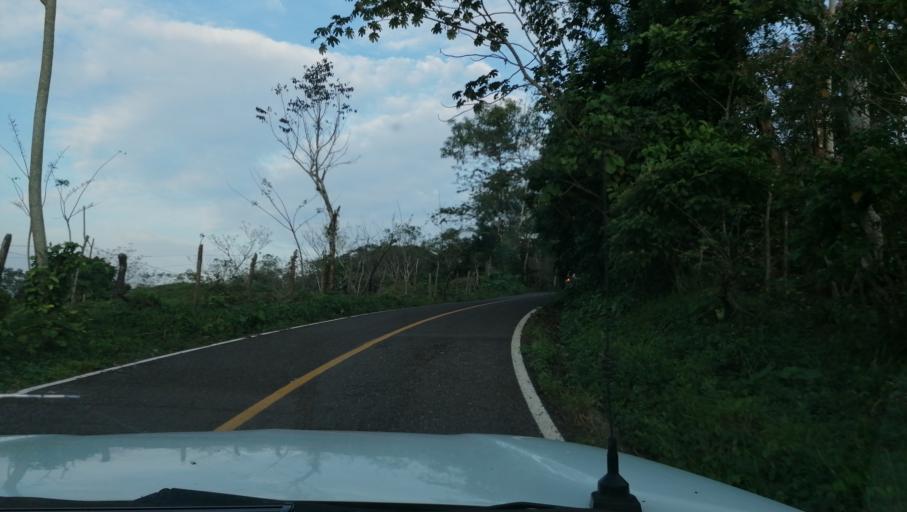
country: MX
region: Chiapas
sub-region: Juarez
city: El Triunfo 1ra. Seccion (Cardona)
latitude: 17.5012
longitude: -93.2404
